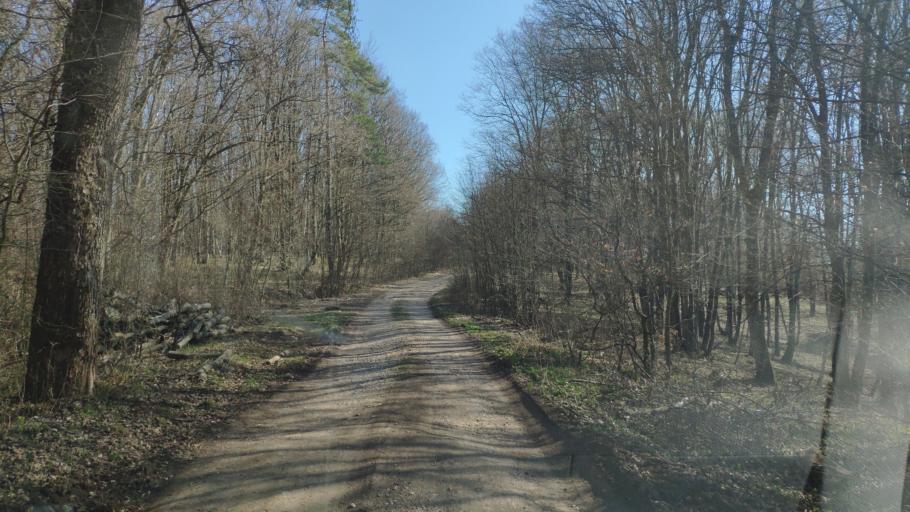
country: SK
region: Kosicky
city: Roznava
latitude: 48.5991
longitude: 20.4107
